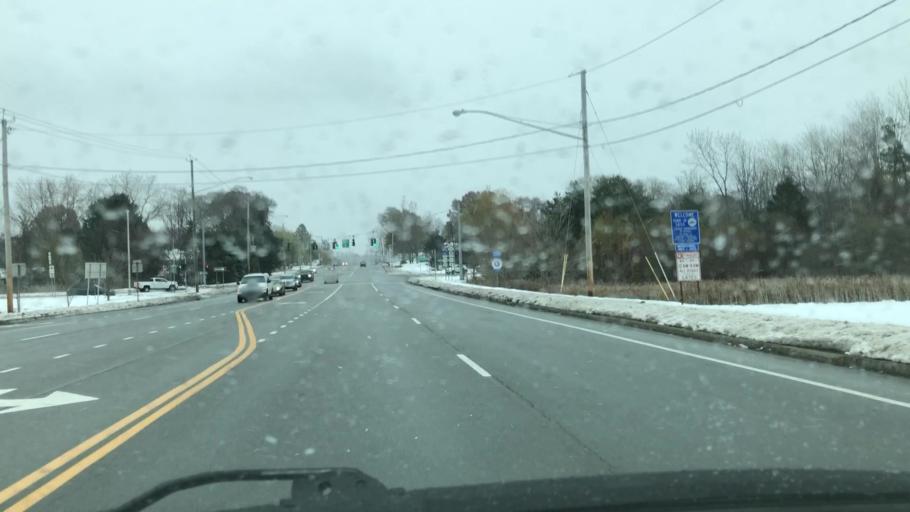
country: US
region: New York
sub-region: Monroe County
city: North Gates
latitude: 43.1259
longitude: -77.7028
